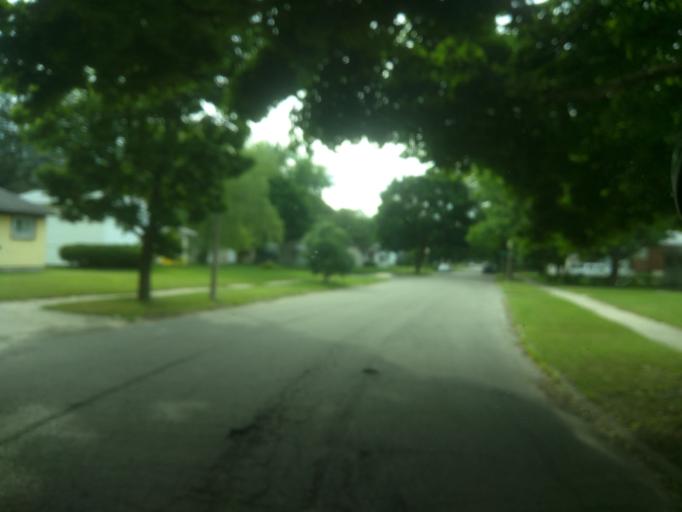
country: US
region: Michigan
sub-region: Eaton County
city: Waverly
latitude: 42.6910
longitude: -84.5980
